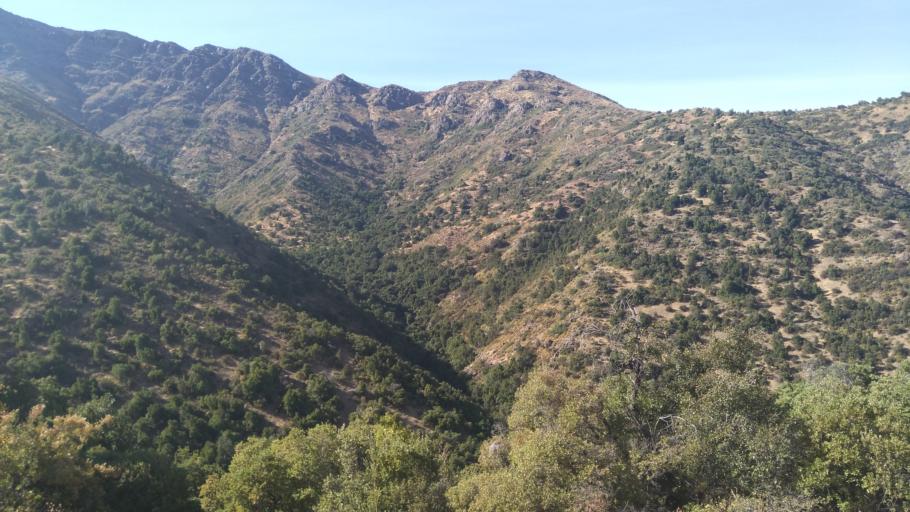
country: CL
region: Santiago Metropolitan
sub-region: Provincia de Cordillera
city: Puente Alto
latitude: -33.7117
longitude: -70.4568
